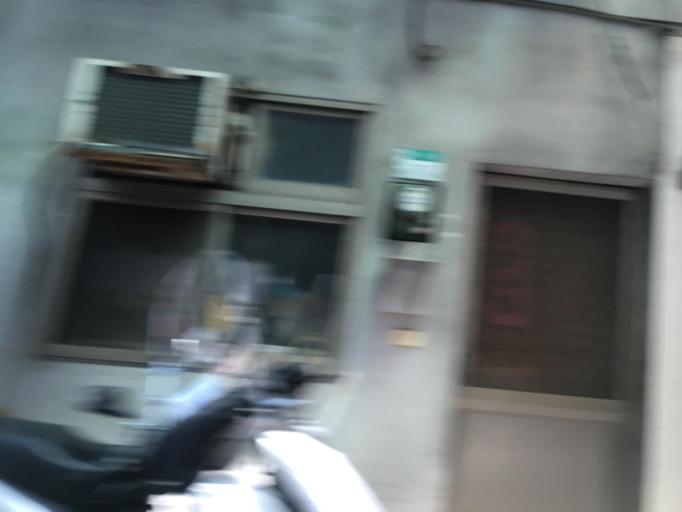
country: TW
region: Taipei
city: Taipei
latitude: 24.9510
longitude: 121.5539
